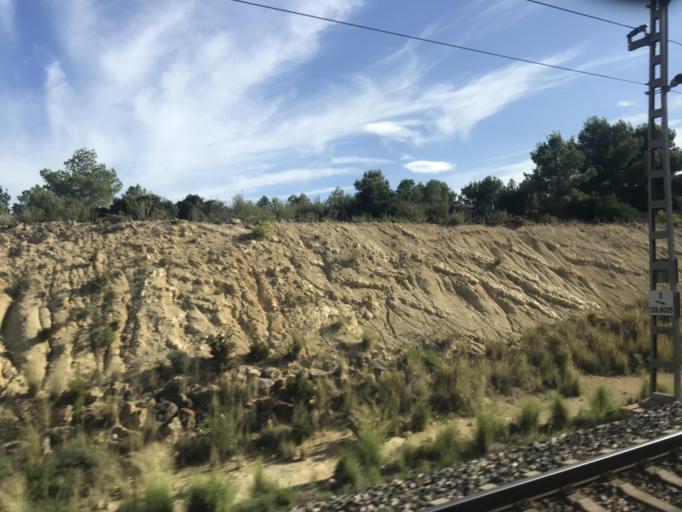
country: ES
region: Catalonia
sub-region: Provincia de Tarragona
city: El Perello
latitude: 40.8516
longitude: 0.7606
